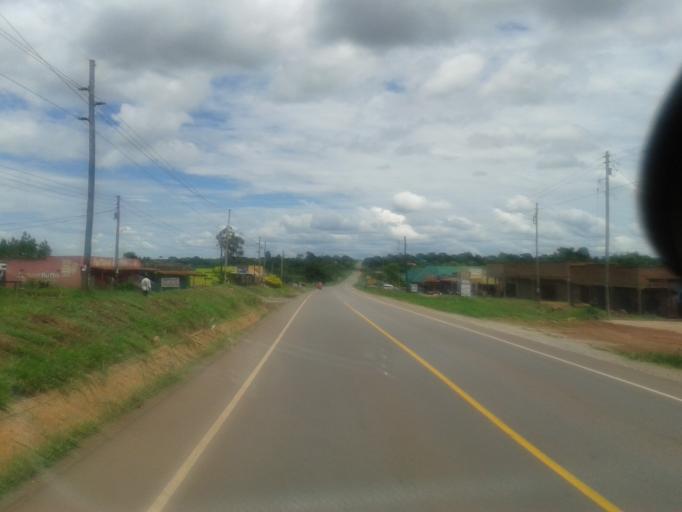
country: UG
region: Western Region
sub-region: Kiryandongo District
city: Kiryandongo
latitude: 1.8747
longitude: 32.0591
